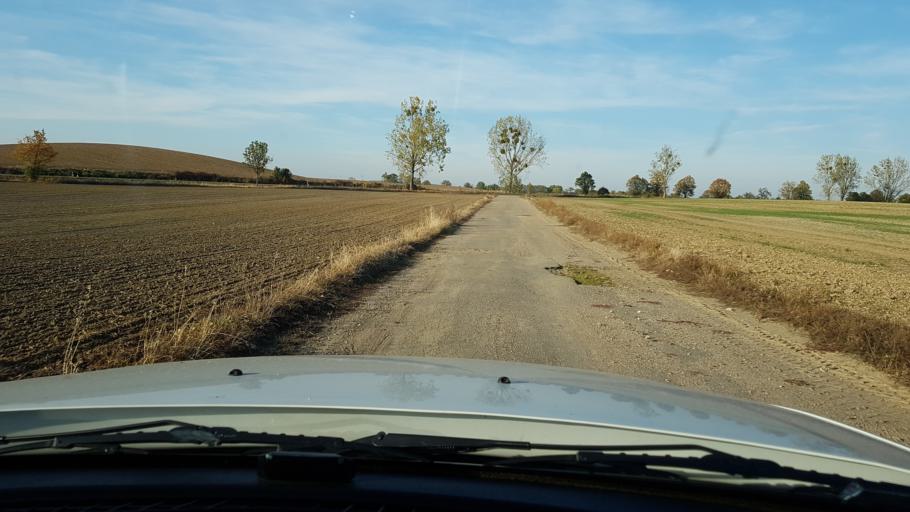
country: PL
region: West Pomeranian Voivodeship
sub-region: Powiat gryfinski
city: Moryn
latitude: 52.8956
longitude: 14.3090
